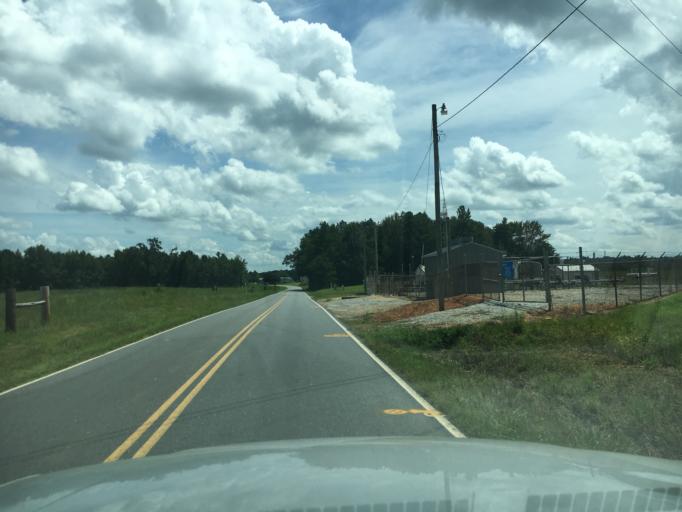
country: US
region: South Carolina
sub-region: Anderson County
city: Belton
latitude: 34.5613
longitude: -82.4695
